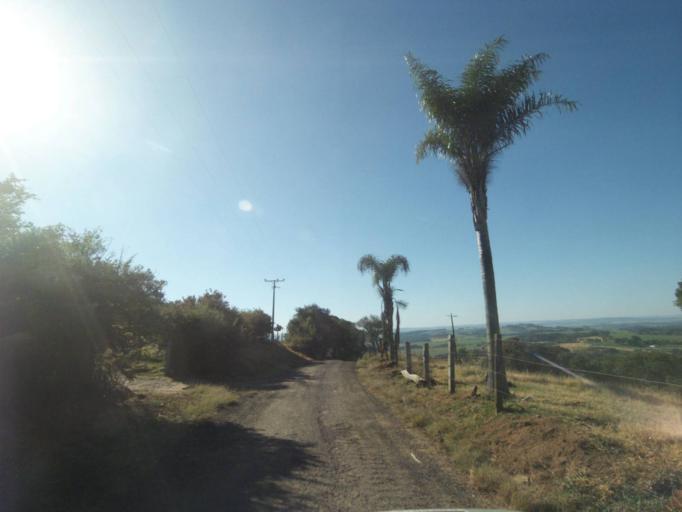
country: BR
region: Parana
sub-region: Tibagi
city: Tibagi
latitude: -24.5426
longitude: -50.4685
